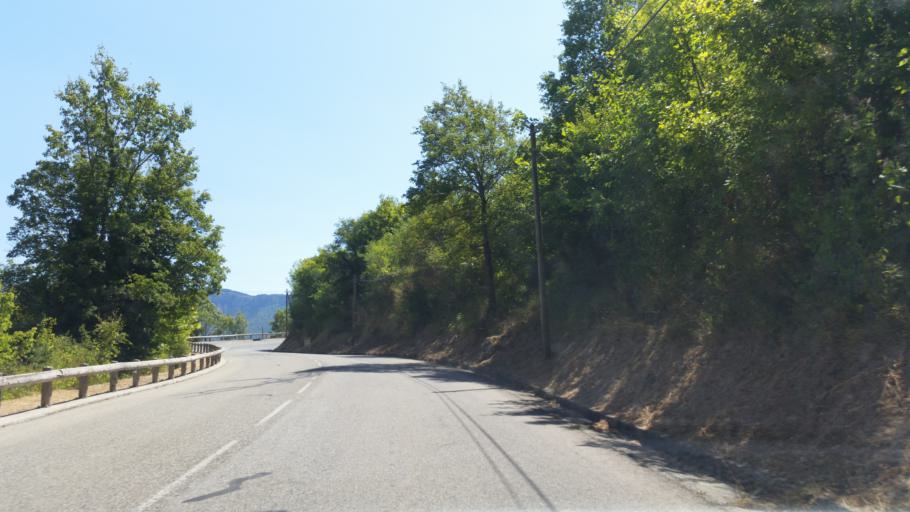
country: FR
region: Provence-Alpes-Cote d'Azur
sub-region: Departement des Alpes-Maritimes
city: Breil-sur-Roya
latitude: 43.9352
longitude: 7.4787
